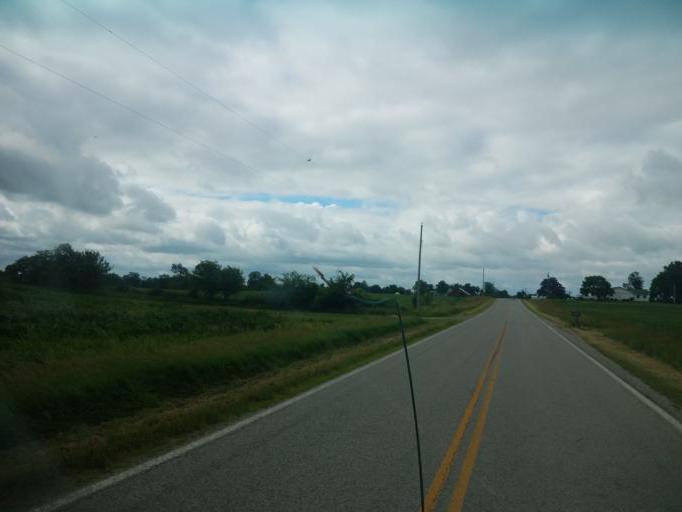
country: US
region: Ohio
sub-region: Champaign County
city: North Lewisburg
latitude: 40.4071
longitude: -83.5172
